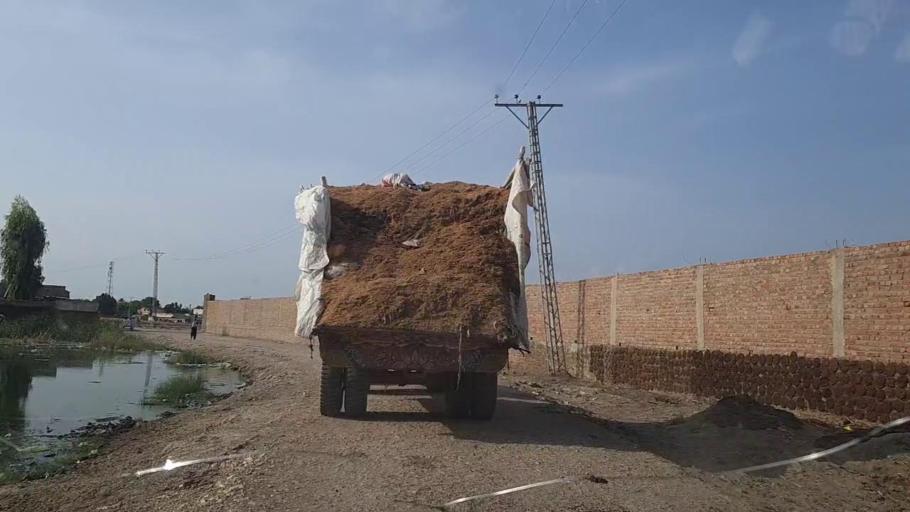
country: PK
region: Sindh
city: Ghotki
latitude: 28.0108
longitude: 69.2951
